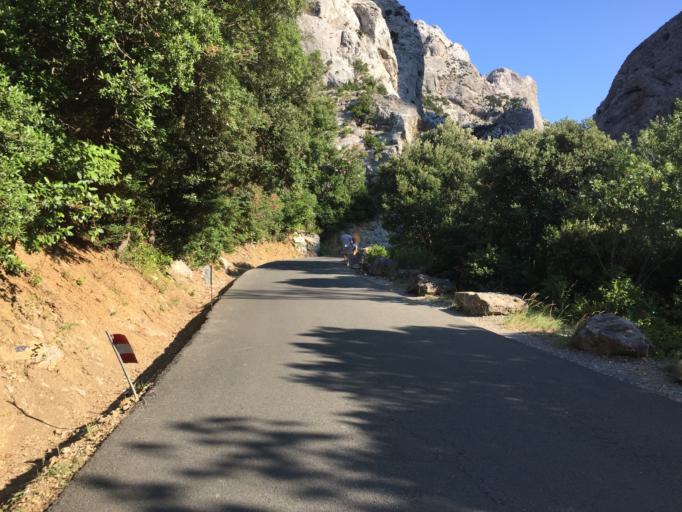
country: FR
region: Languedoc-Roussillon
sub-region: Departement des Pyrenees-Orientales
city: Saint-Paul-de-Fenouillet
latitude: 42.8457
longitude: 2.4780
